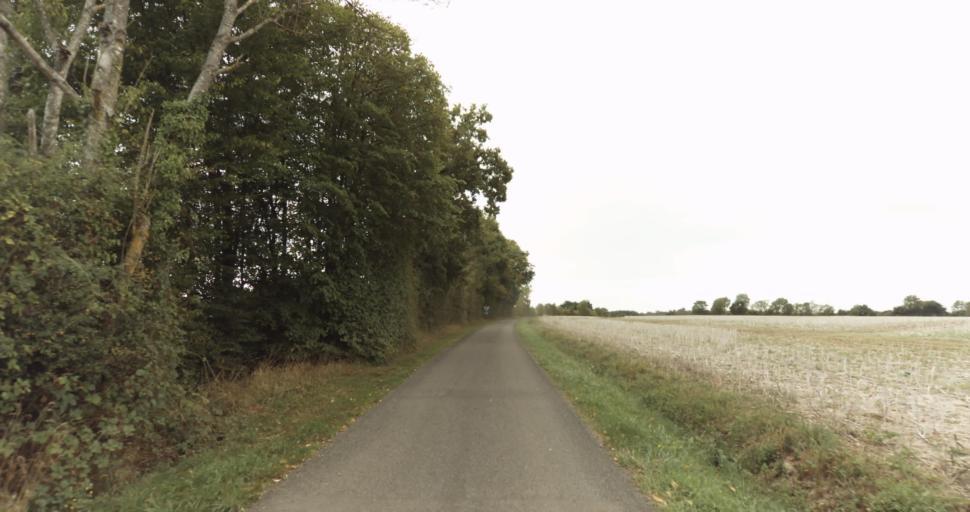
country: FR
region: Lower Normandy
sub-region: Departement de l'Orne
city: Sainte-Gauburge-Sainte-Colombe
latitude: 48.7284
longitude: 0.4322
